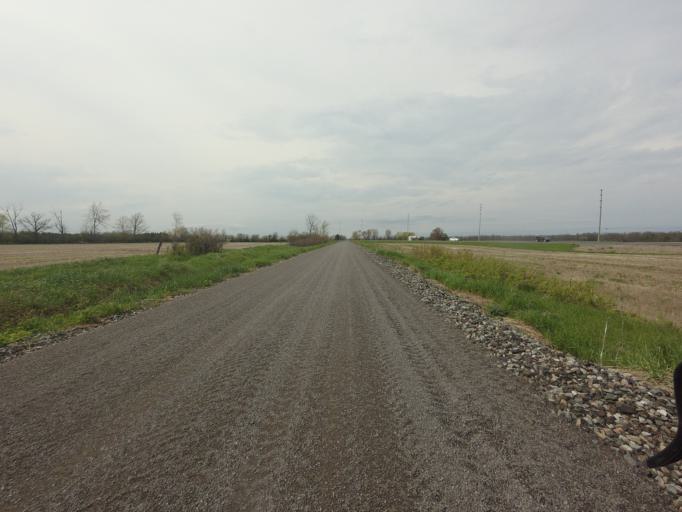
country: CA
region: Ontario
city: Carleton Place
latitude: 45.1818
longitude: -76.1572
